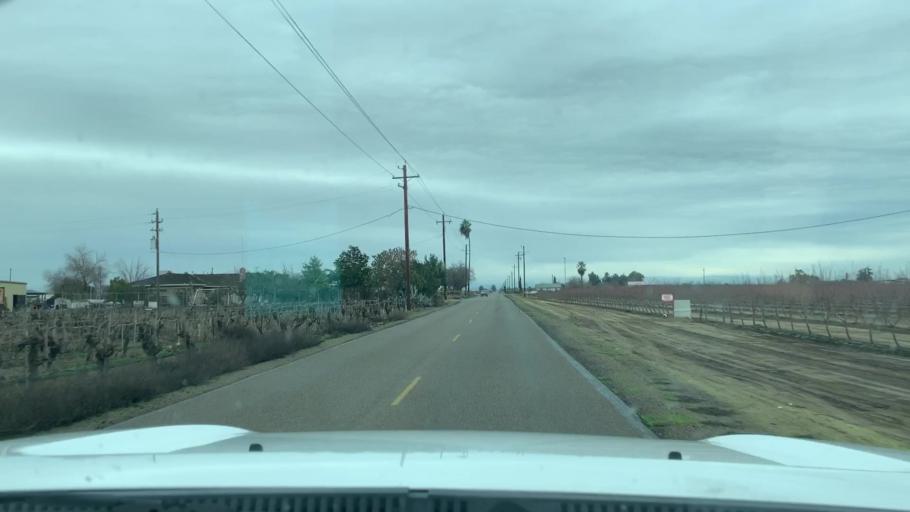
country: US
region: California
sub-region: Fresno County
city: Caruthers
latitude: 36.5474
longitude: -119.7757
